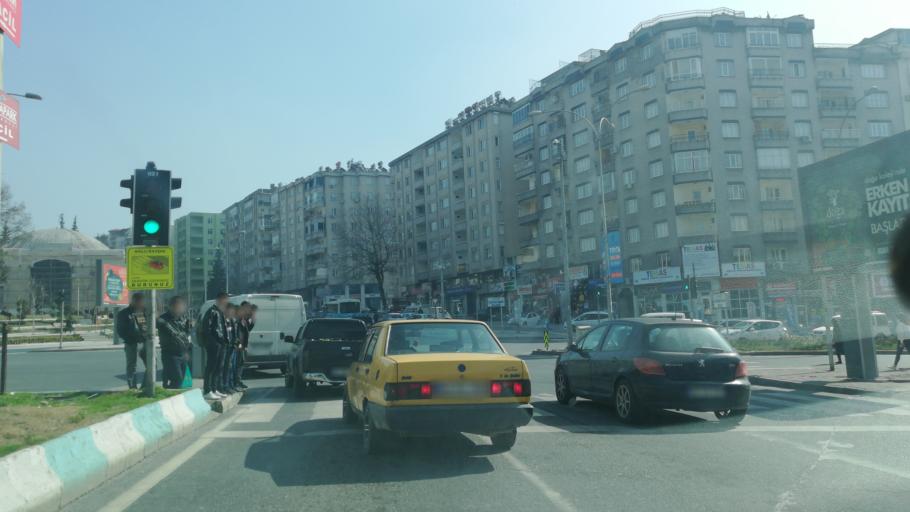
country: TR
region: Kahramanmaras
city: Kahramanmaras
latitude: 37.5748
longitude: 36.9257
